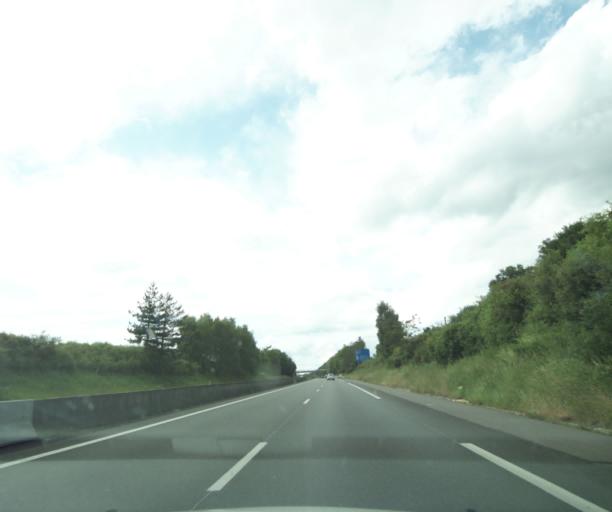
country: FR
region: Centre
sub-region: Departement du Cher
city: Vierzon
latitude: 47.2311
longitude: 2.0997
